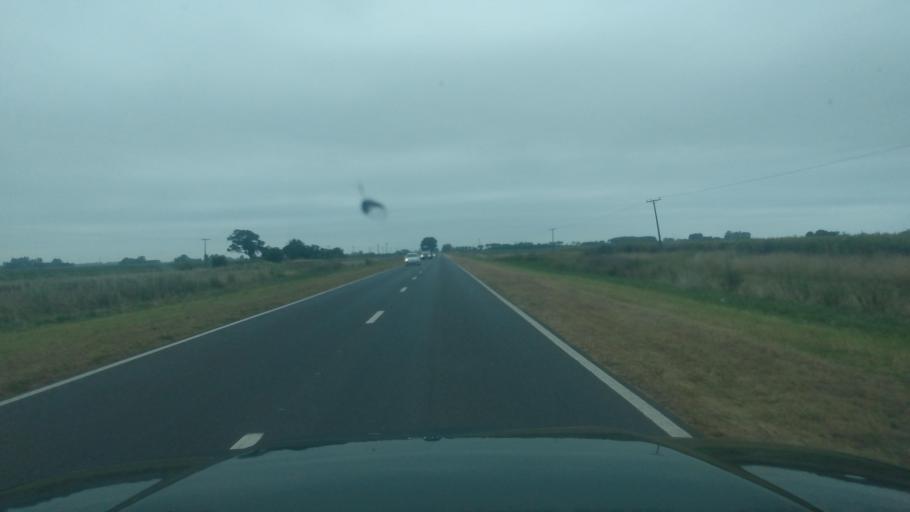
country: AR
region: Buenos Aires
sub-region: Partido de Bragado
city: Bragado
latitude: -35.2050
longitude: -60.5297
